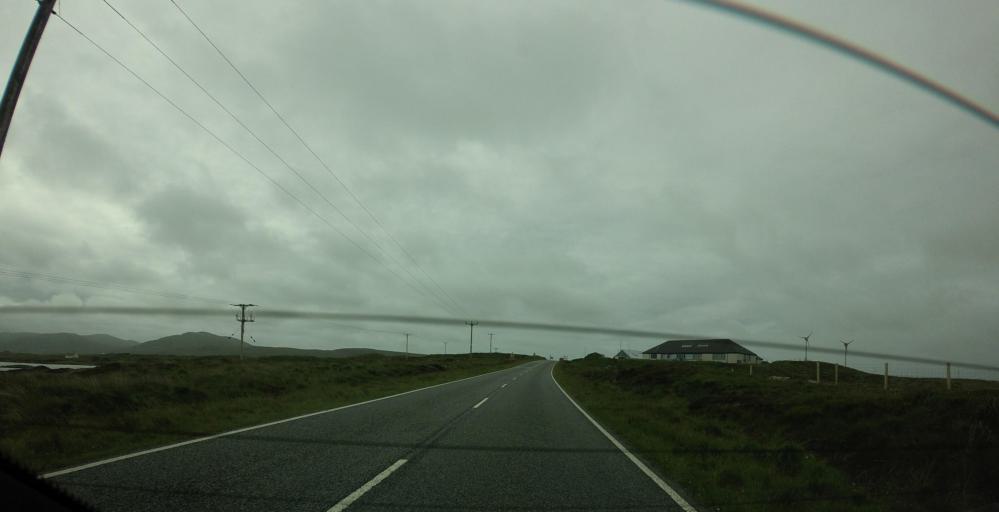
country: GB
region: Scotland
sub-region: Eilean Siar
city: Isle of South Uist
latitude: 57.2515
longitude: -7.3771
